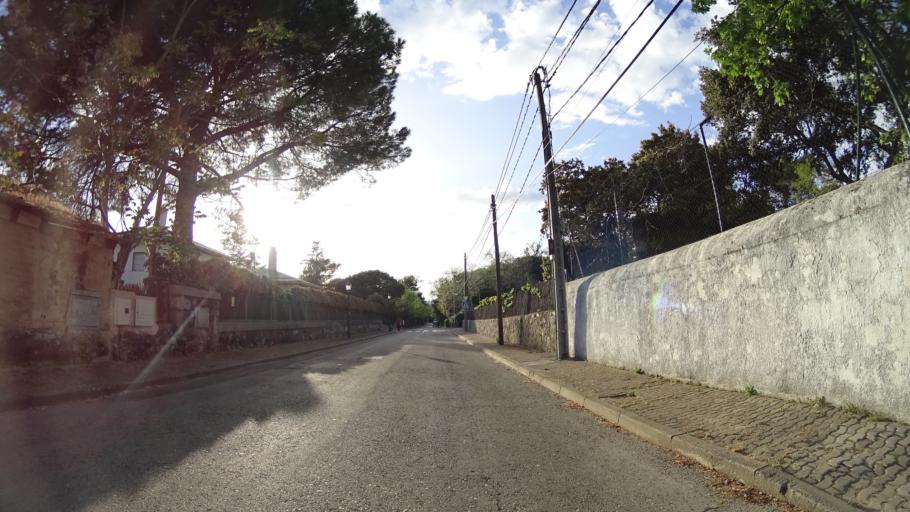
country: ES
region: Madrid
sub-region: Provincia de Madrid
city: Torrelodones
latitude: 40.5829
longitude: -3.9559
